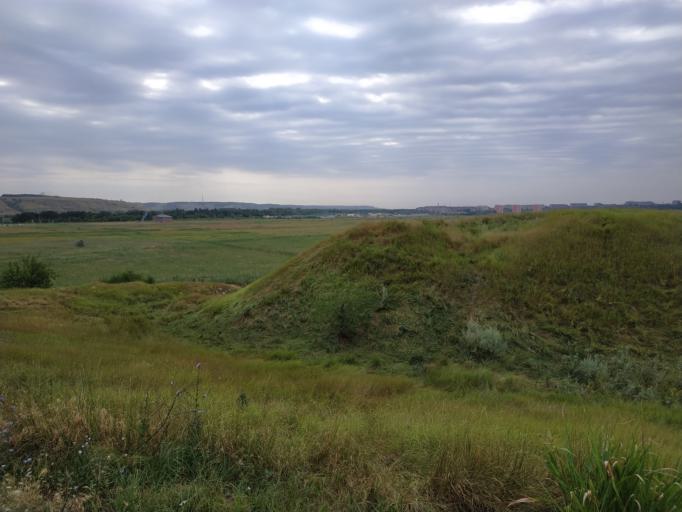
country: RU
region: Krasnodarskiy
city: Krasnaya Polyana
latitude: 45.0263
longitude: 41.1045
